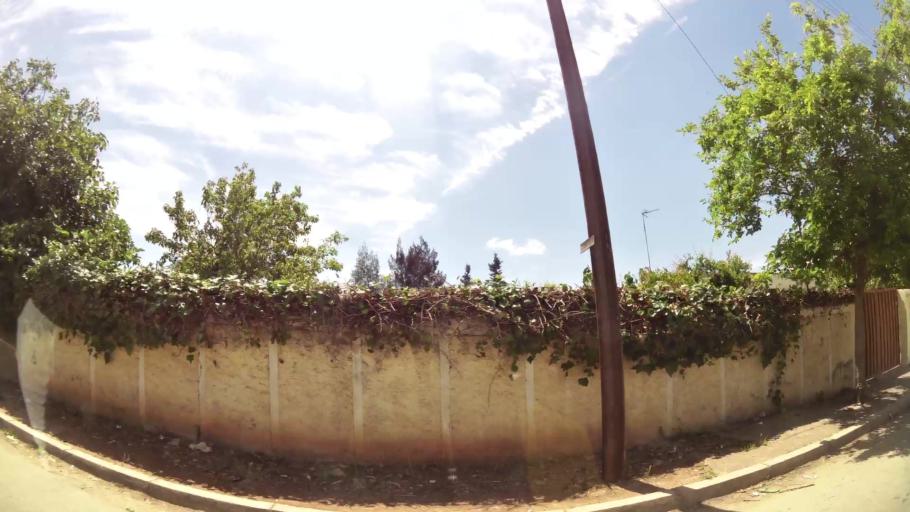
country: MA
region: Fes-Boulemane
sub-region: Fes
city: Fes
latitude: 34.0096
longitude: -4.9931
